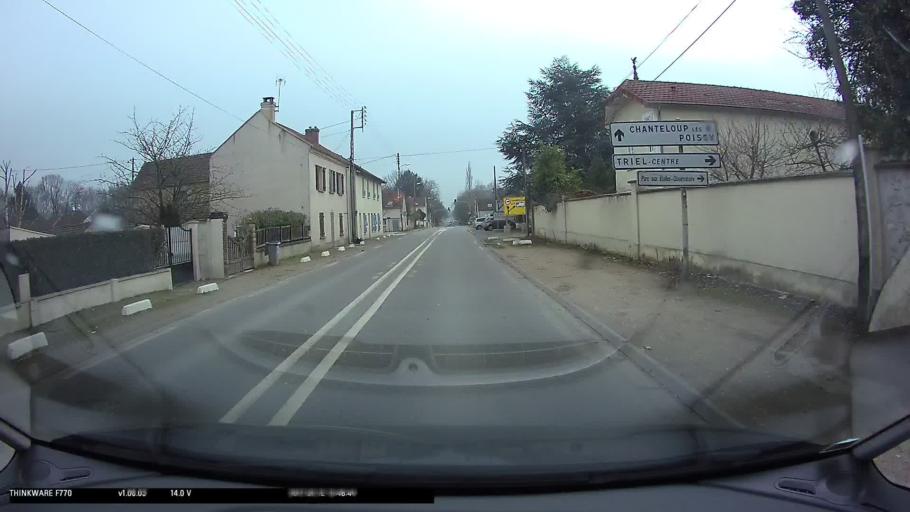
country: FR
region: Ile-de-France
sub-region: Departement des Yvelines
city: Triel-sur-Seine
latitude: 49.0042
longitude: 2.0103
